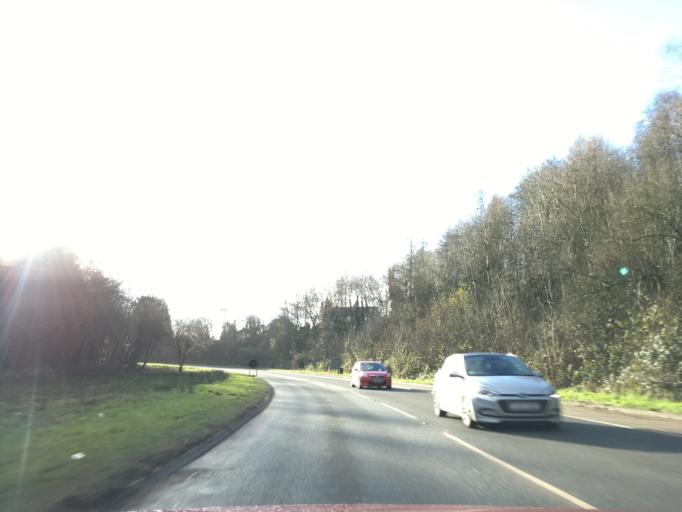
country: GB
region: Wales
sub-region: Caerphilly County Borough
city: Llanbradach
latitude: 51.5908
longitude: -3.2300
